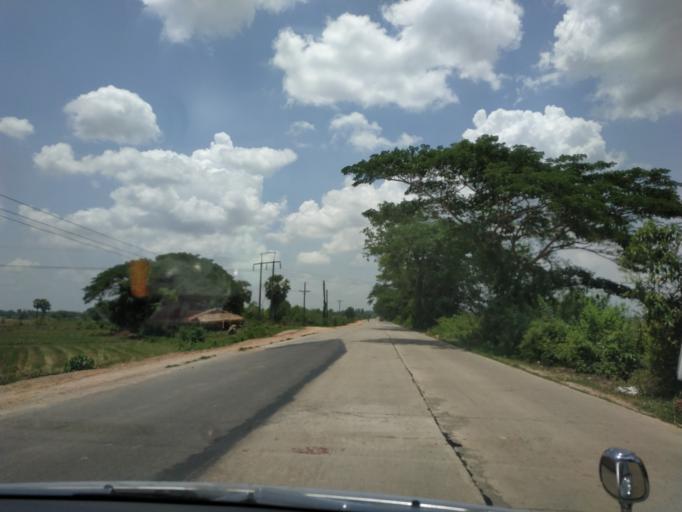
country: MM
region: Bago
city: Bago
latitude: 17.4784
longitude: 96.4972
